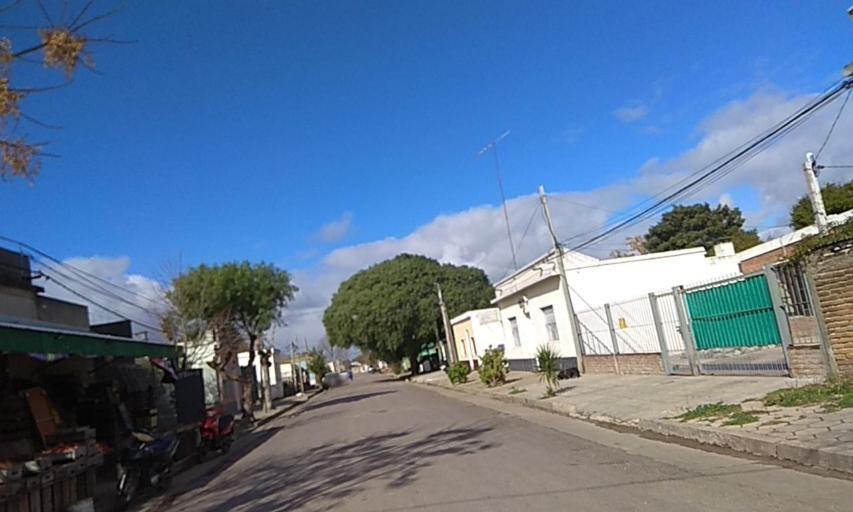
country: UY
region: Florida
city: Florida
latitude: -34.1054
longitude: -56.2145
